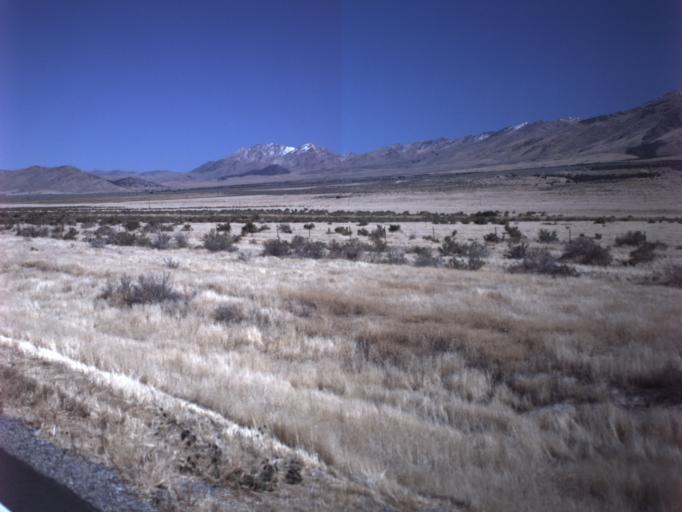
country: US
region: Utah
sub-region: Tooele County
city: Grantsville
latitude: 40.4684
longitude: -112.7466
